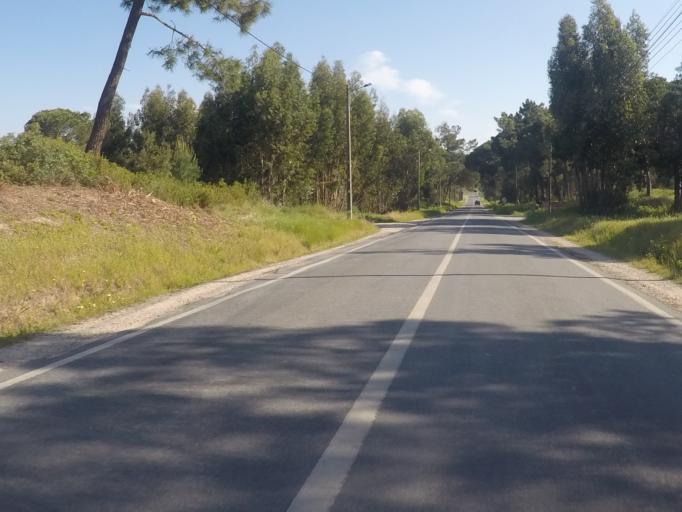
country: PT
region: Setubal
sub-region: Sesimbra
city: Sesimbra
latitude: 38.4825
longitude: -9.1600
